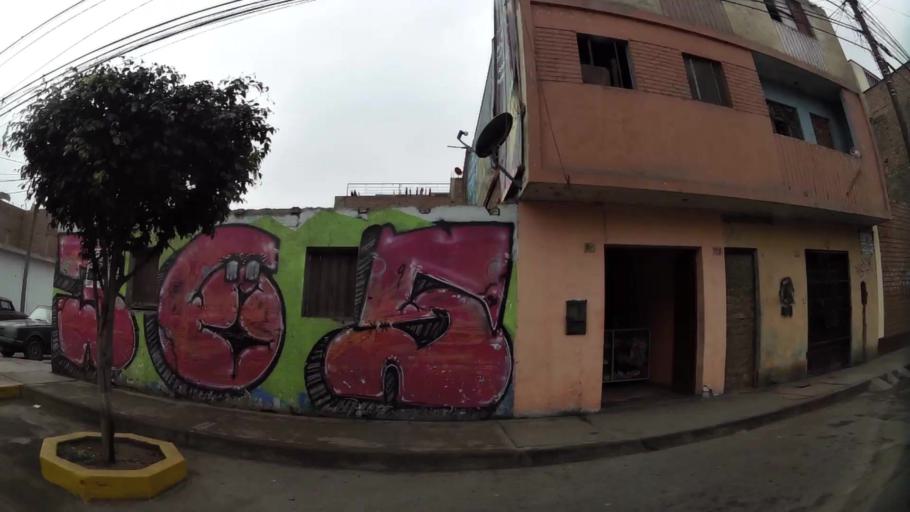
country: PE
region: Lima
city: Lima
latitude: -12.0520
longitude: -77.0082
